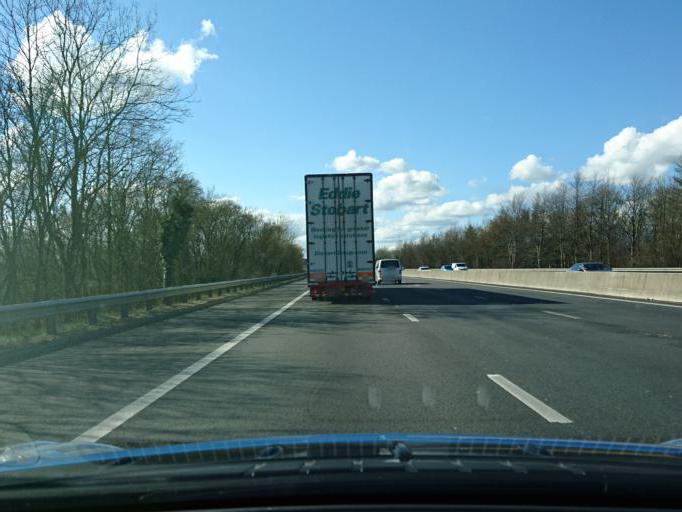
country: GB
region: England
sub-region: West Berkshire
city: Lambourn
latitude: 51.4691
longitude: -1.5188
